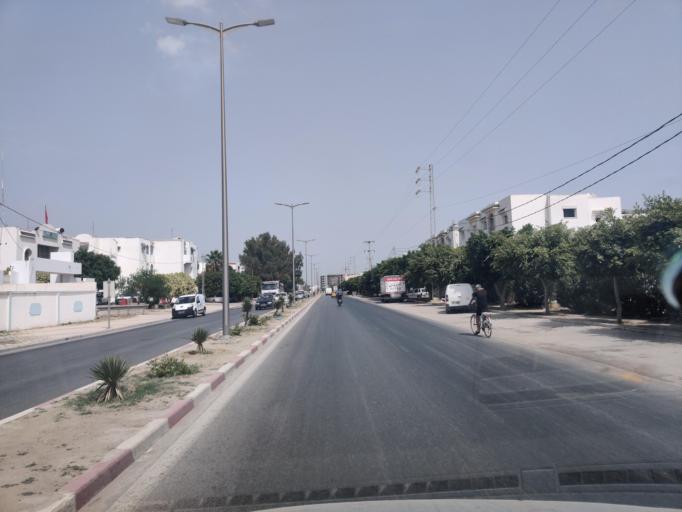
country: TN
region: Nabul
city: Bu `Urqub
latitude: 36.5884
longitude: 10.5057
